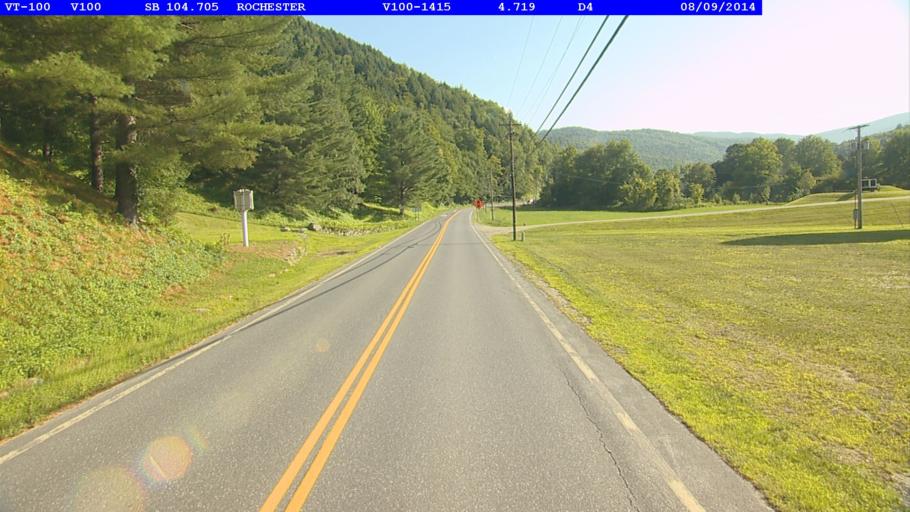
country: US
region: Vermont
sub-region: Orange County
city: Randolph
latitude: 43.8664
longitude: -72.8086
